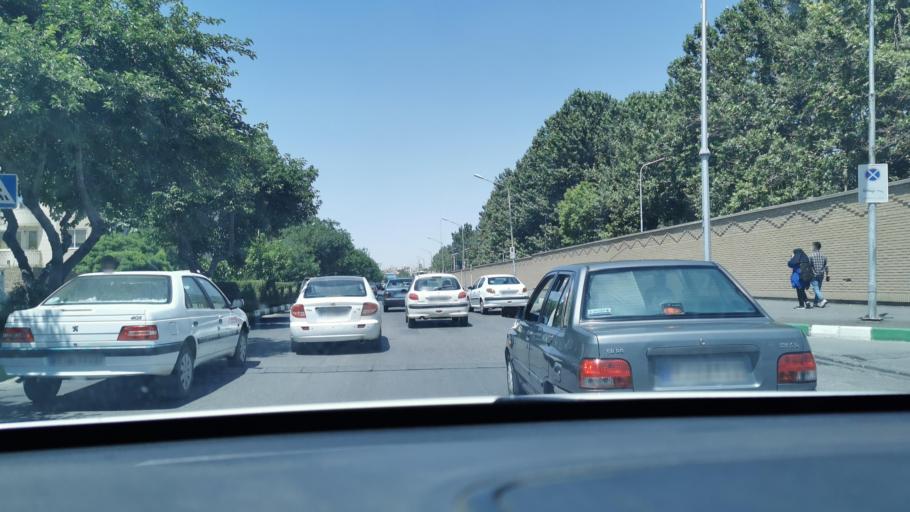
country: IR
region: Razavi Khorasan
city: Mashhad
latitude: 36.3348
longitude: 59.4868
